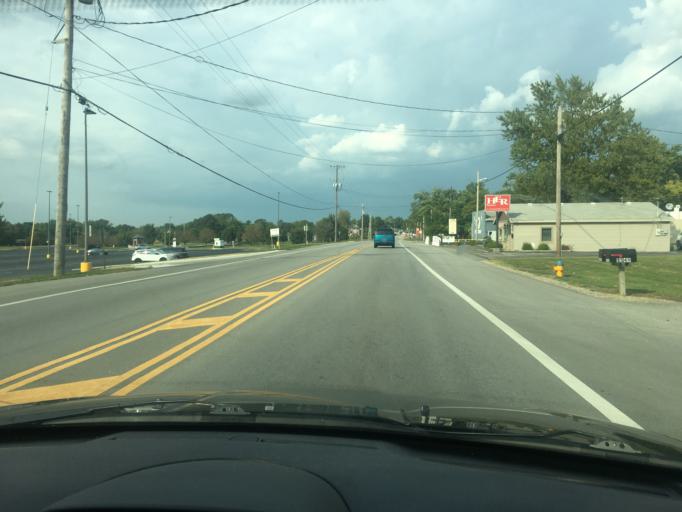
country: US
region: Ohio
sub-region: Champaign County
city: Urbana
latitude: 40.0896
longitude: -83.7568
